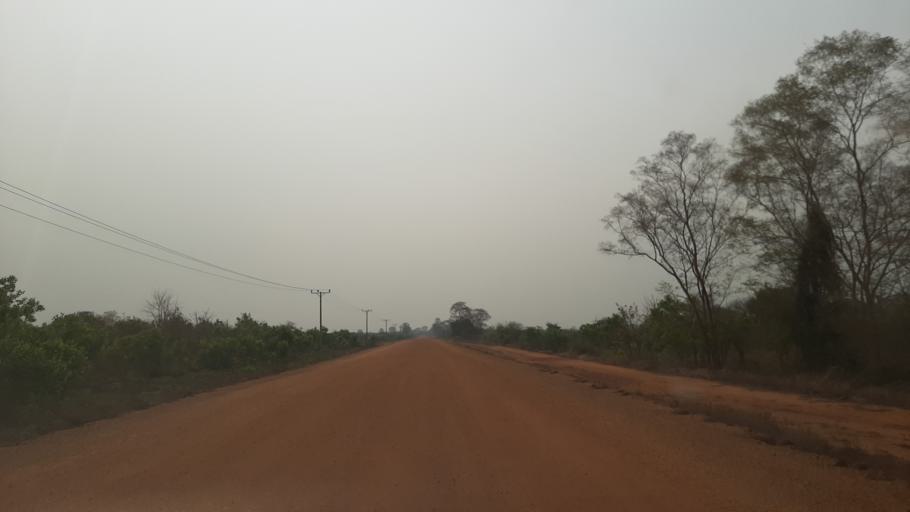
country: ET
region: Gambela
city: Gambela
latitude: 8.1321
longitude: 34.2916
